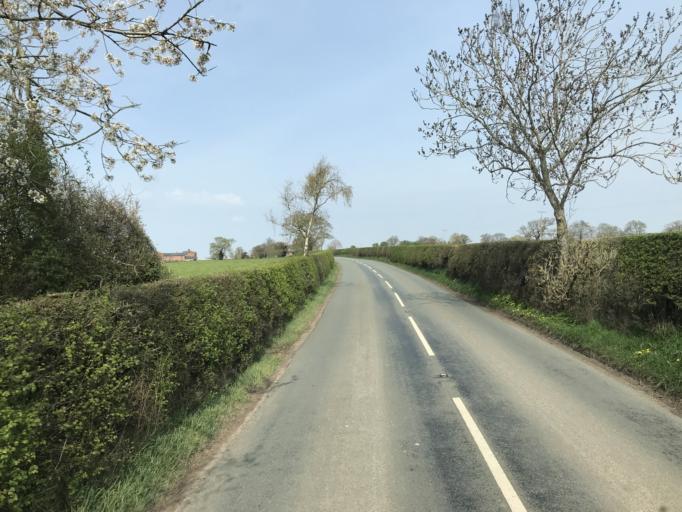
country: GB
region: England
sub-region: Cheshire West and Chester
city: Eccleston
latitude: 53.1546
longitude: -2.8622
